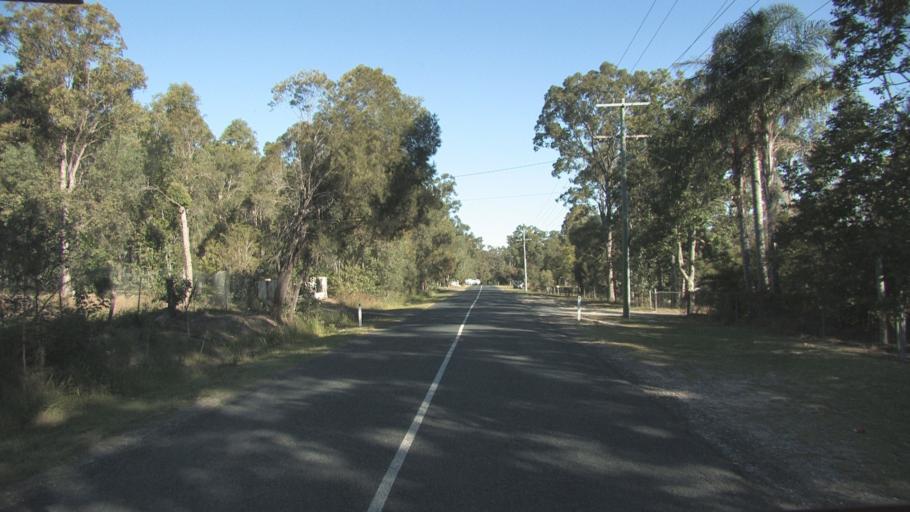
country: AU
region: Queensland
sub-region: Logan
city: Logan Reserve
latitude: -27.7379
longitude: 153.1032
